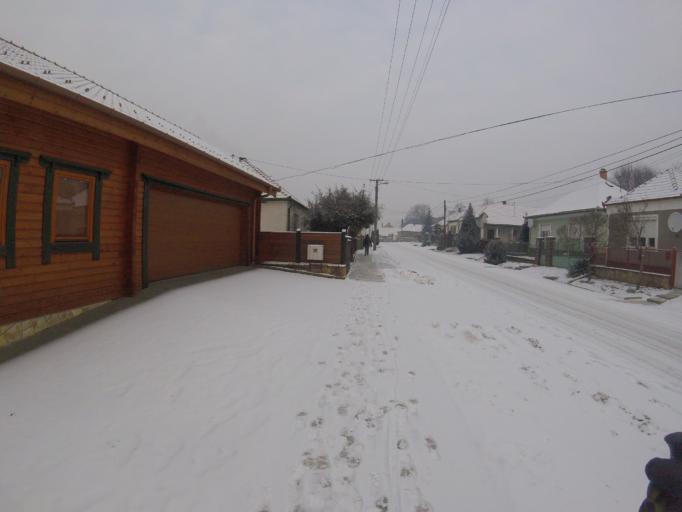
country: HU
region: Heves
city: Sirok
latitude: 47.9327
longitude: 20.1926
